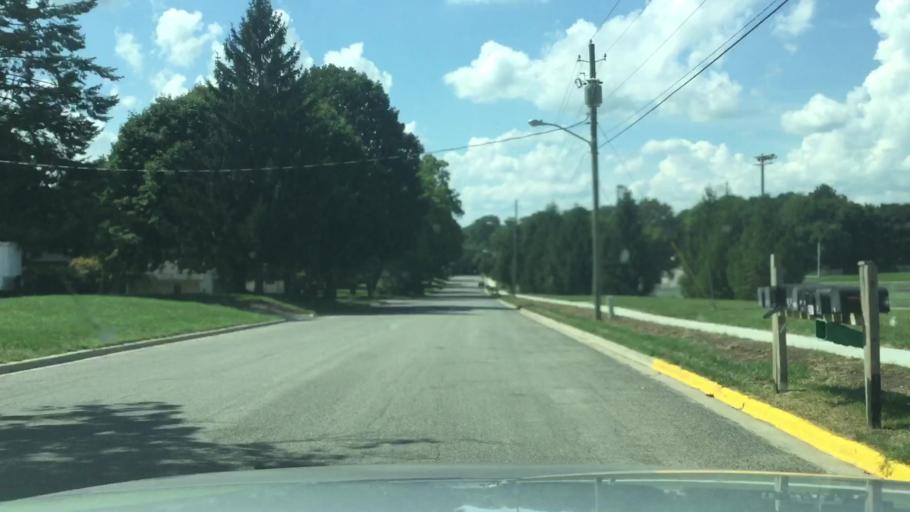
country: US
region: Michigan
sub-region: Lenawee County
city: Clinton
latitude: 42.0723
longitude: -83.9631
